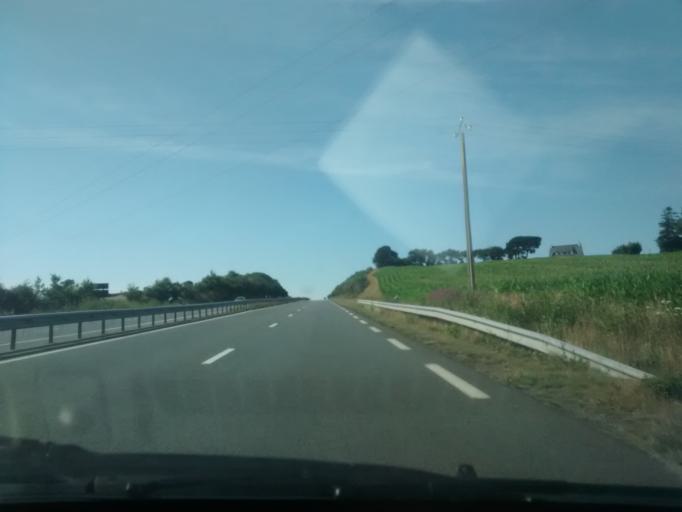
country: FR
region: Brittany
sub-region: Departement des Cotes-d'Armor
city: Rospez
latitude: 48.6973
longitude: -3.3735
